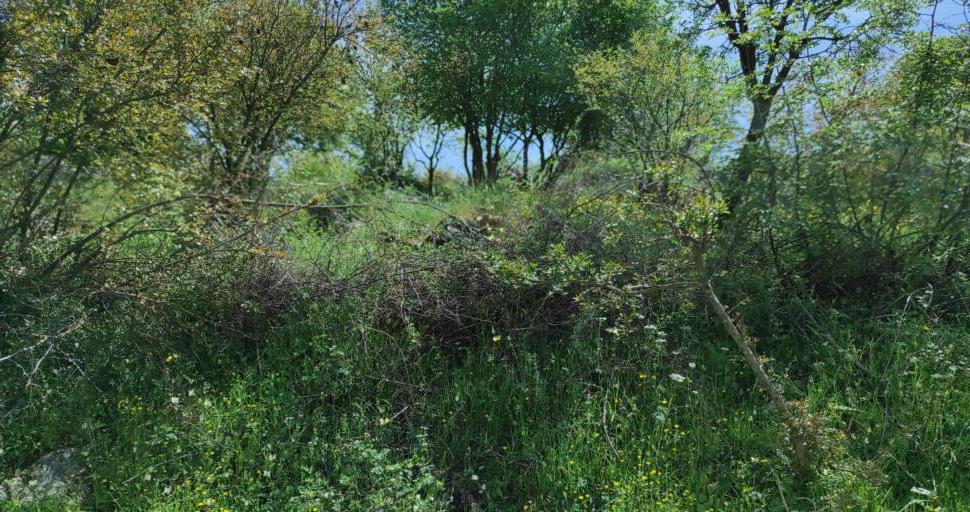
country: AL
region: Shkoder
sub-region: Rrethi i Malesia e Madhe
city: Gruemire
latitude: 42.1400
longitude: 19.5470
